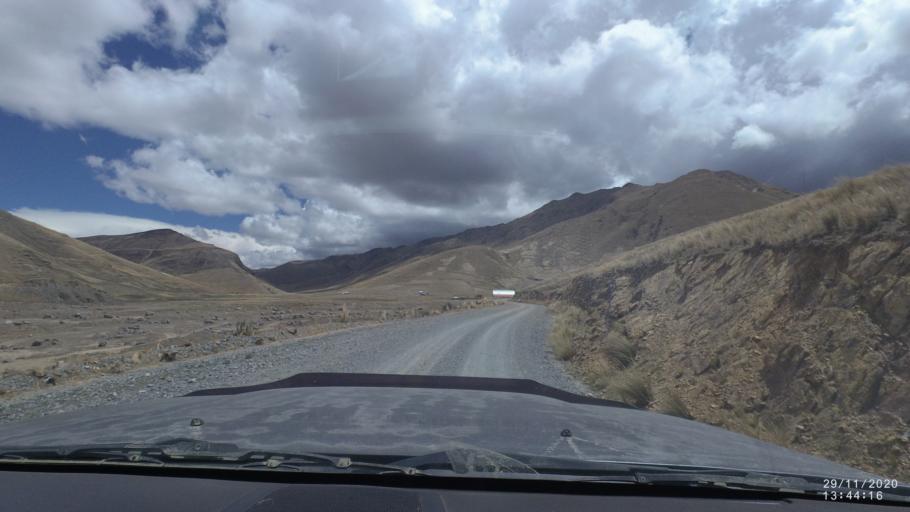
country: BO
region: Cochabamba
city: Cochabamba
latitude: -17.1443
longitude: -66.3176
